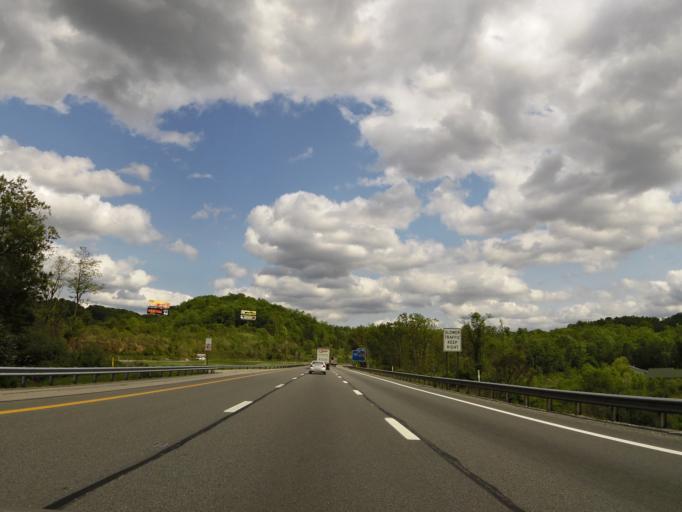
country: US
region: West Virginia
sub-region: Raleigh County
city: Prosperity
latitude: 37.8441
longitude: -81.2341
